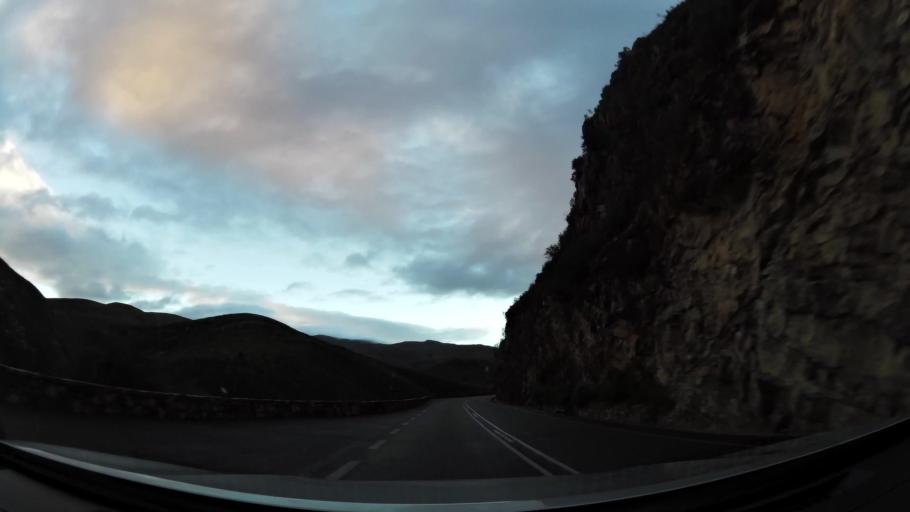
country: ZA
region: Western Cape
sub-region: Overberg District Municipality
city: Swellendam
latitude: -33.9908
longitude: 20.7069
